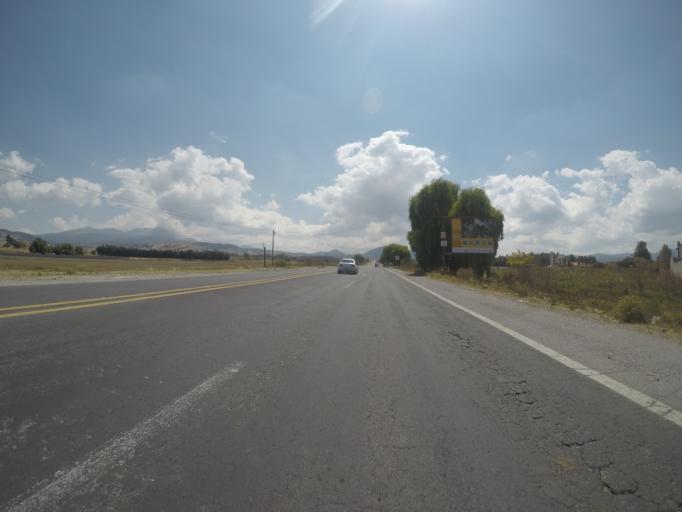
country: MX
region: Mexico
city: San Juan de las Huertas
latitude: 19.2385
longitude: -99.7731
